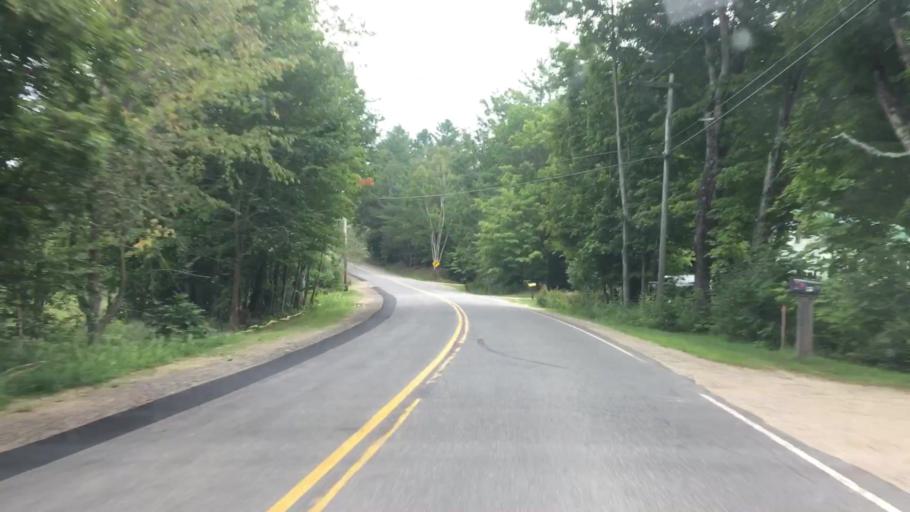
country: US
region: Maine
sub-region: Oxford County
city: Rumford
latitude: 44.5253
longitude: -70.6829
